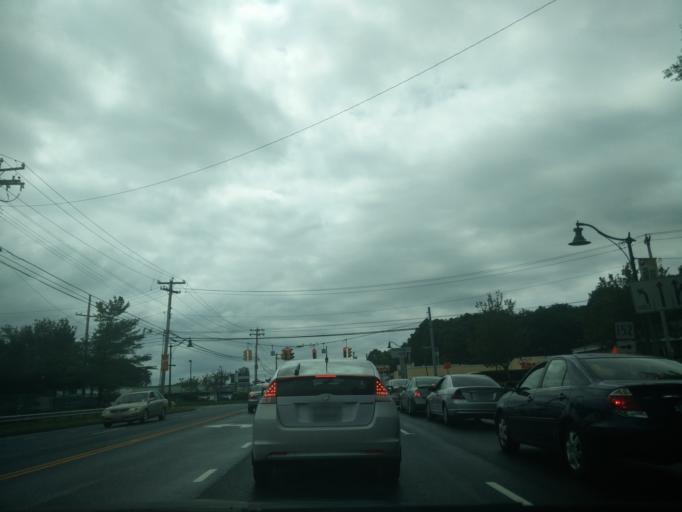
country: US
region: Connecticut
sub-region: New Haven County
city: Orange
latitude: 41.2584
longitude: -73.0119
